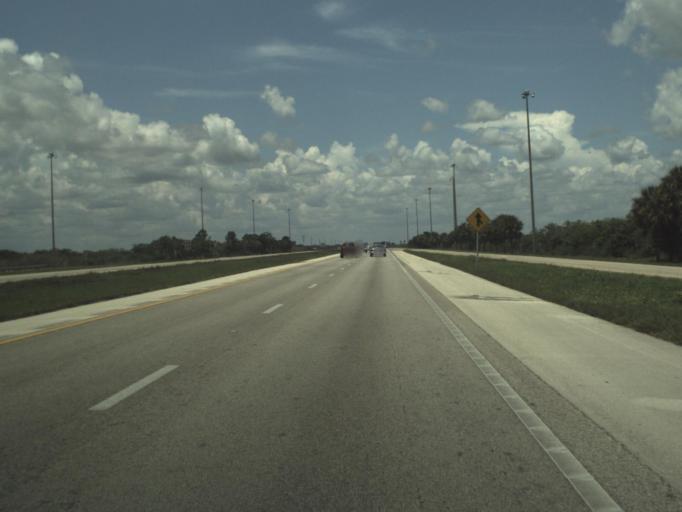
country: US
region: Florida
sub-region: Broward County
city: Weston
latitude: 26.1466
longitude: -80.6398
